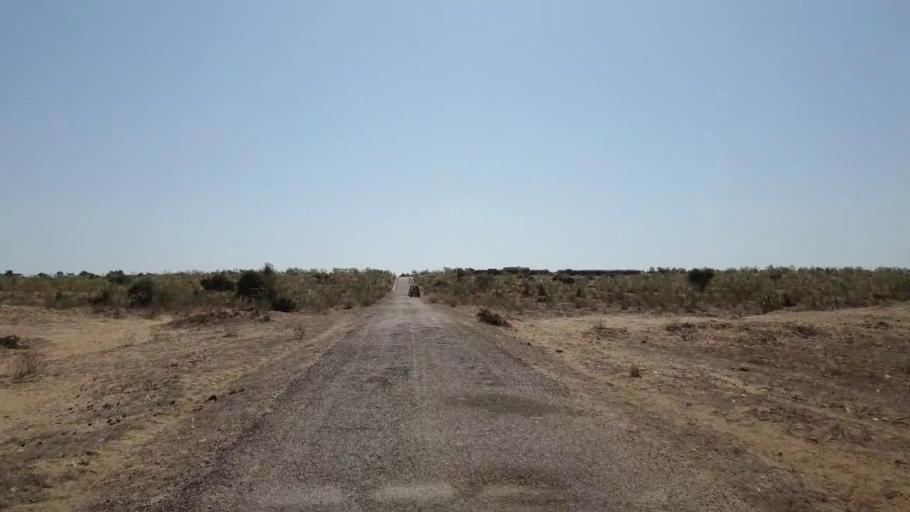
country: PK
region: Sindh
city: Nabisar
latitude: 25.0786
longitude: 69.9812
